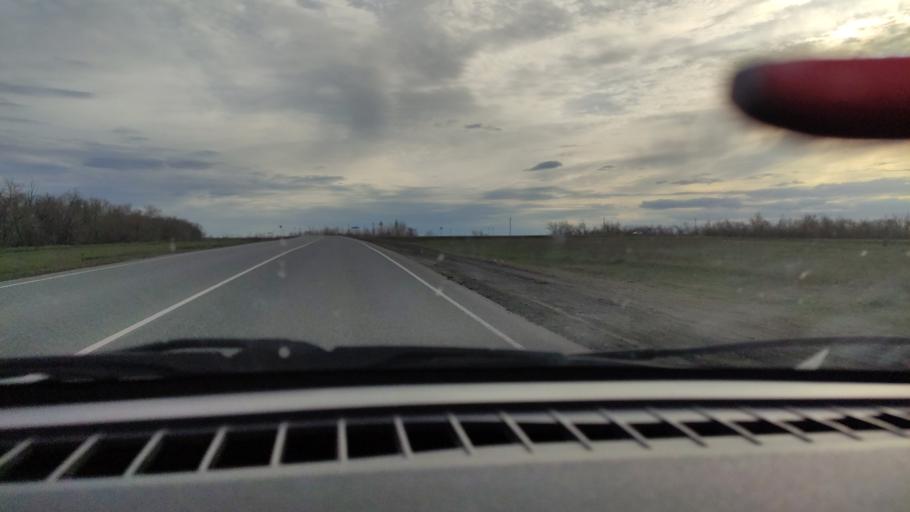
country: RU
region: Orenburg
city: Tatarskaya Kargala
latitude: 52.0200
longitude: 55.2133
